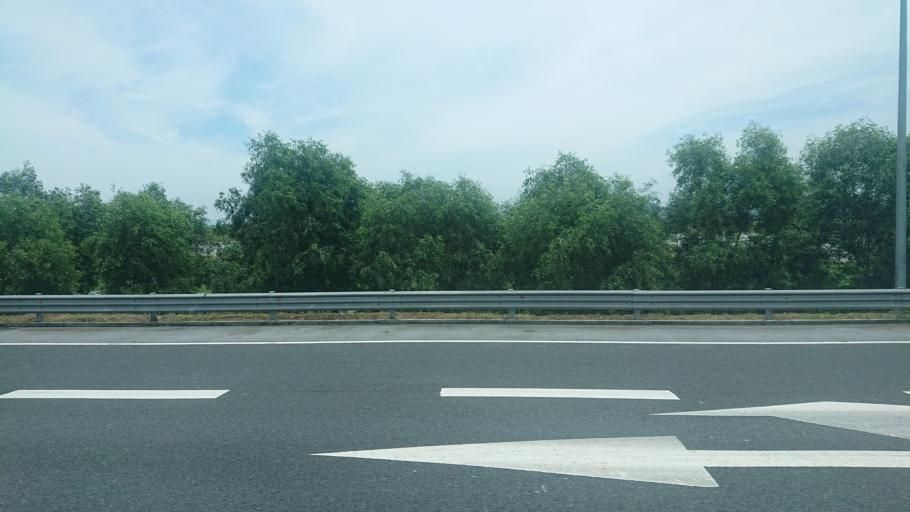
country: VN
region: Hai Phong
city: An Lao
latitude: 20.7921
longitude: 106.5504
